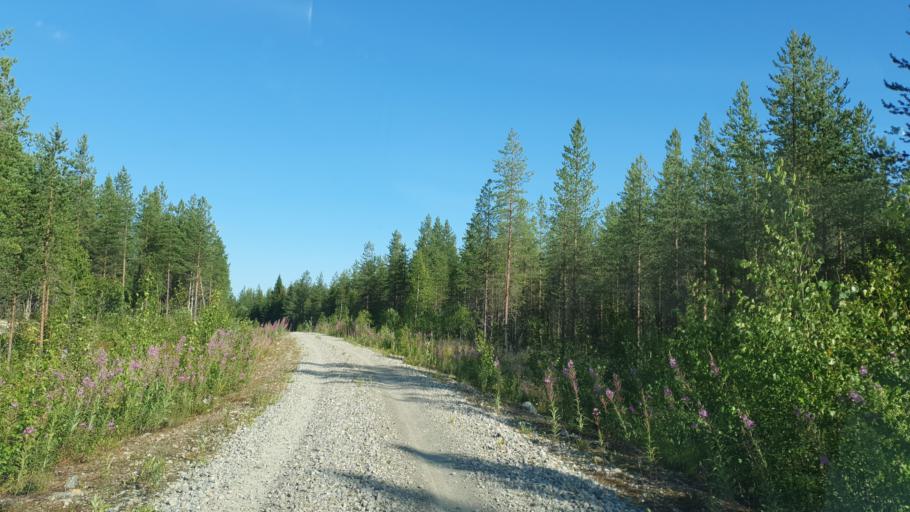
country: FI
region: Kainuu
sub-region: Kehys-Kainuu
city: Kuhmo
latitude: 64.0028
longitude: 29.7650
